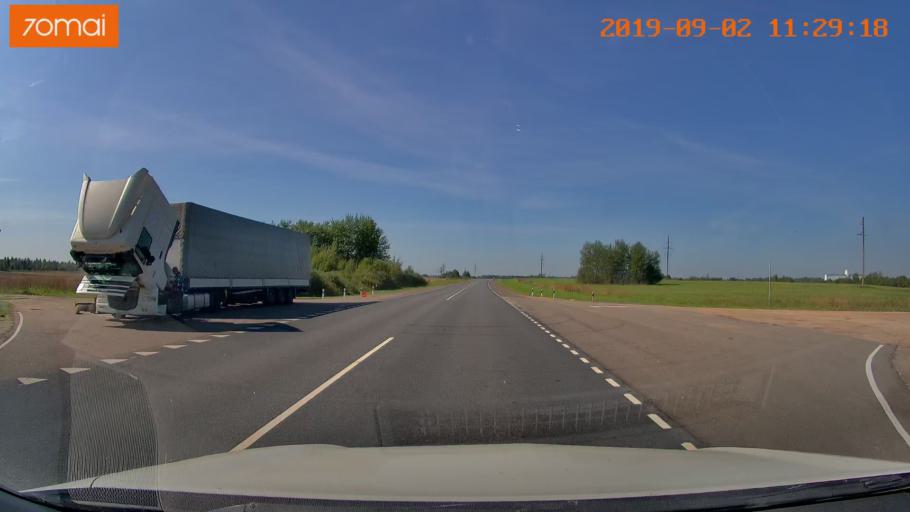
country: RU
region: Smolensk
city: Roslavl'
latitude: 53.9896
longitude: 32.8675
